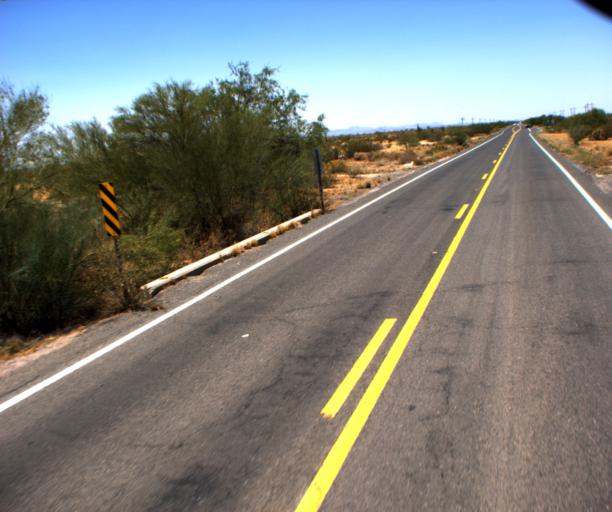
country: US
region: Arizona
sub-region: Pinal County
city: Florence
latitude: 32.9126
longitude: -111.2899
